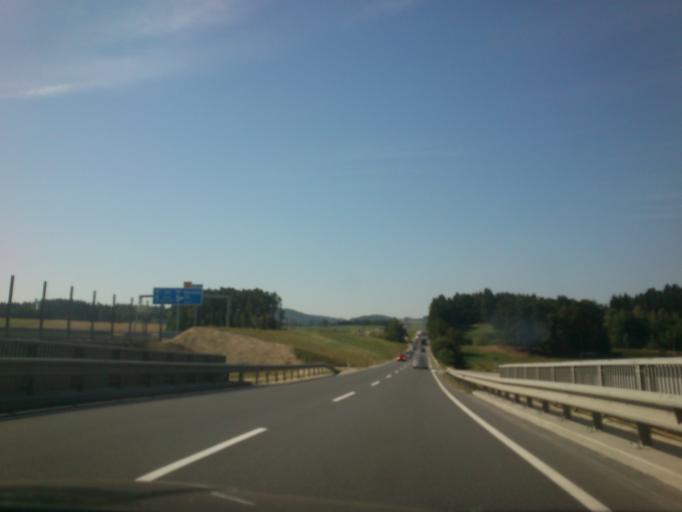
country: AT
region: Upper Austria
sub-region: Politischer Bezirk Freistadt
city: Freistadt
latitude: 48.4630
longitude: 14.5021
